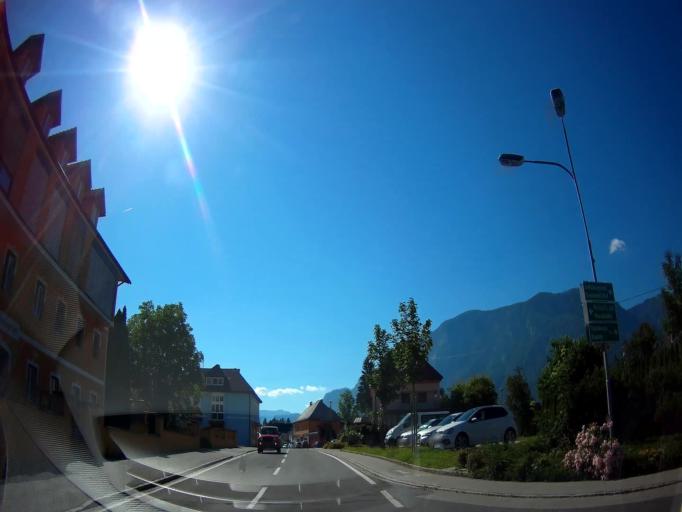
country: AT
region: Carinthia
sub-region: Politischer Bezirk Volkermarkt
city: Gallizien
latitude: 46.5597
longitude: 14.5065
